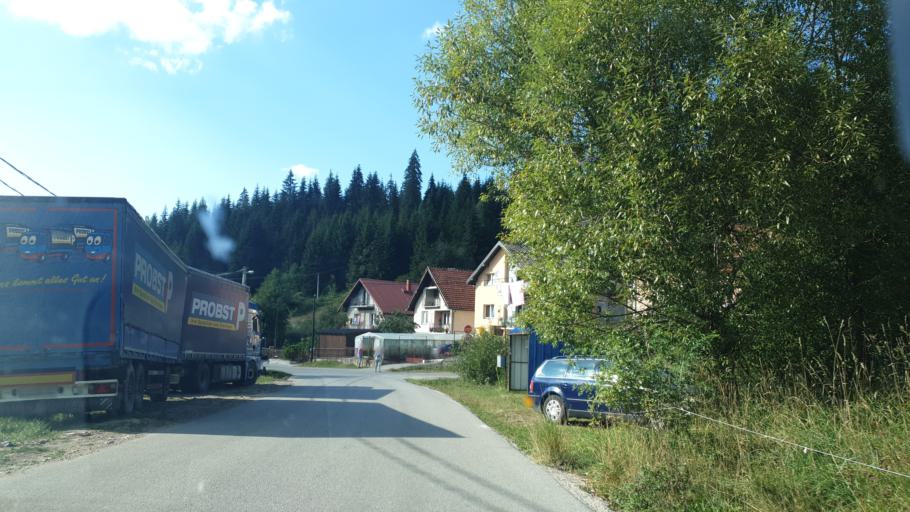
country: RS
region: Central Serbia
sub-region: Zlatiborski Okrug
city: Nova Varos
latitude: 43.4494
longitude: 19.8488
